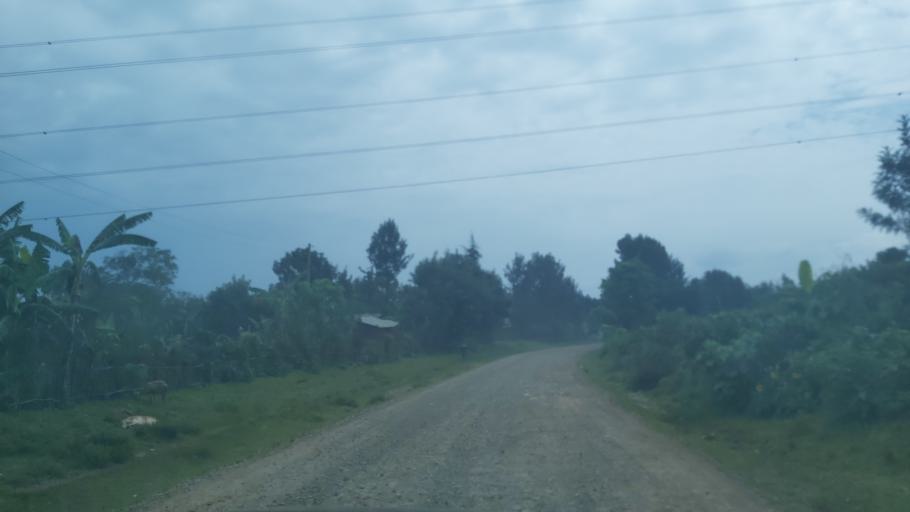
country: ET
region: Oromiya
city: Jima
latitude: 7.7368
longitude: 36.7705
